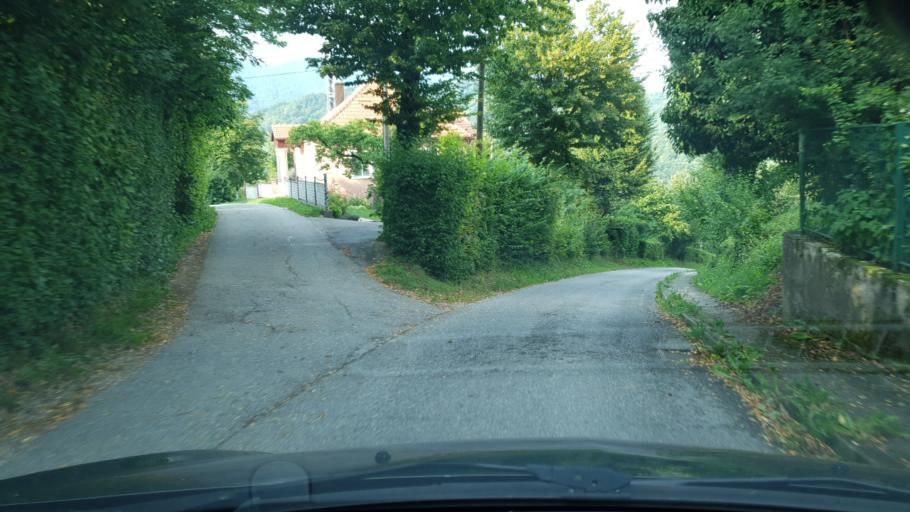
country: HR
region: Krapinsko-Zagorska
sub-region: Grad Krapina
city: Krapina
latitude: 46.1619
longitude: 15.8622
